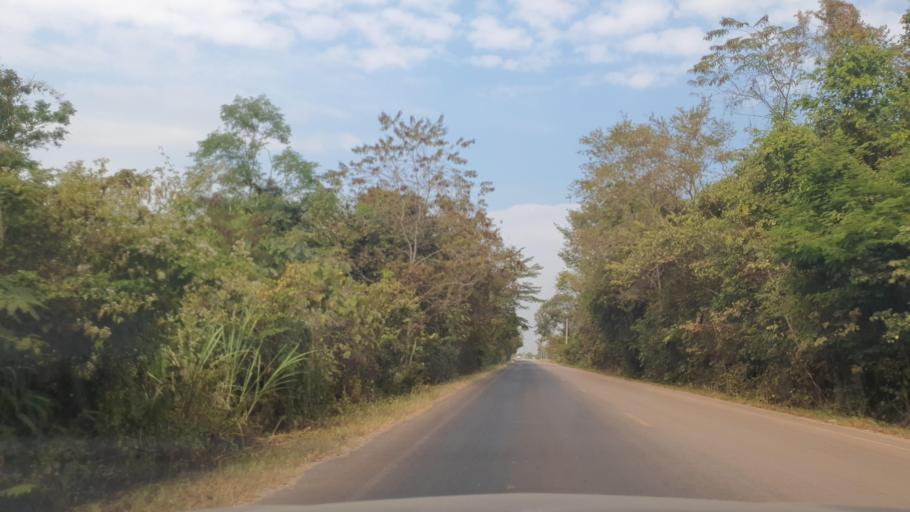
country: TH
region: Changwat Bueng Kan
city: Si Wilai
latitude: 18.2921
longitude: 103.8217
